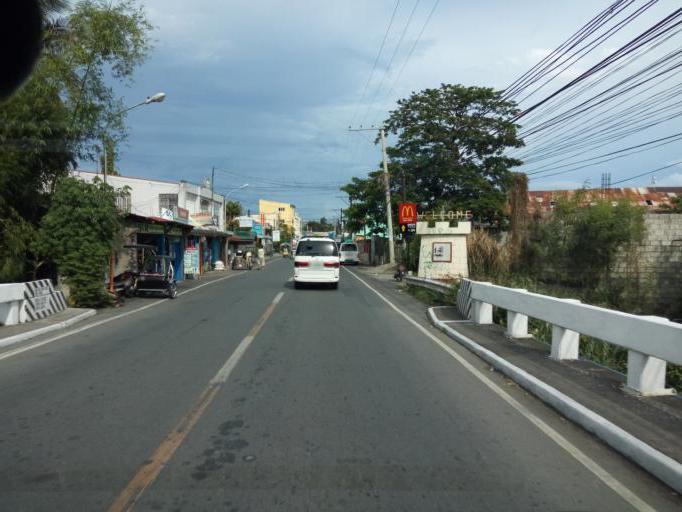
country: PH
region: Central Luzon
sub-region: Province of Nueva Ecija
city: Sibul
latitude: 15.7949
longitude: 120.9876
